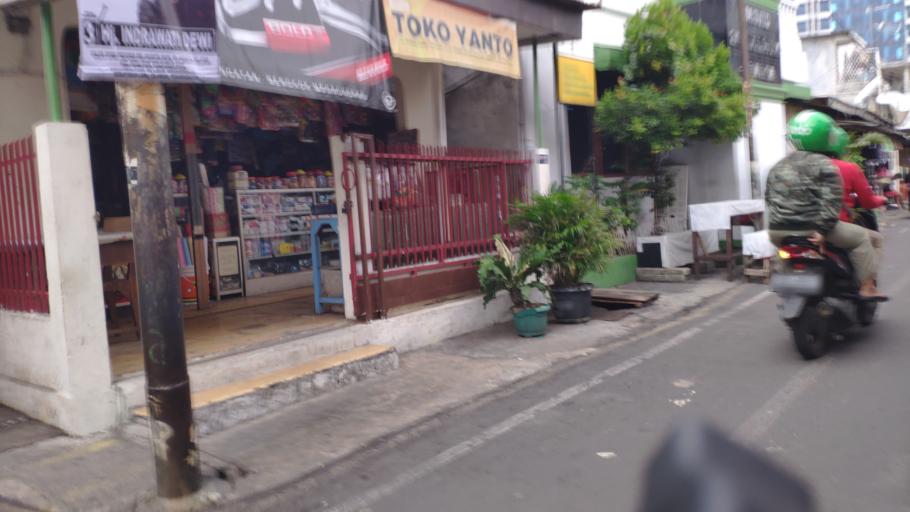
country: ID
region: Jakarta Raya
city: Jakarta
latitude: -6.2204
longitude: 106.8422
